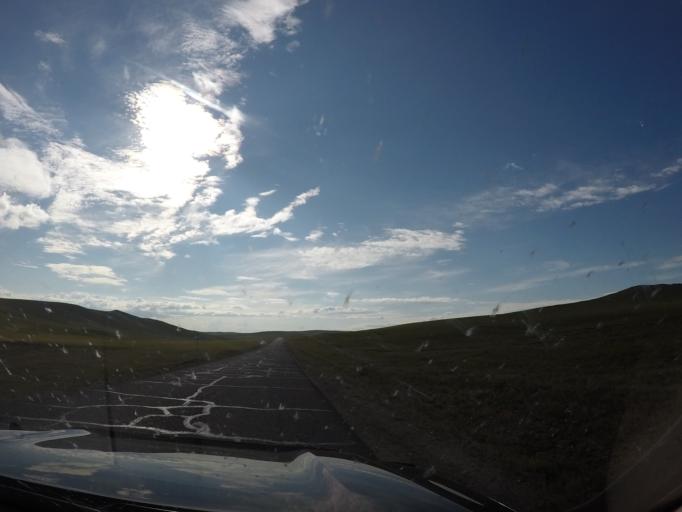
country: MN
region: Hentiy
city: Modot
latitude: 47.8056
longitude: 108.7292
